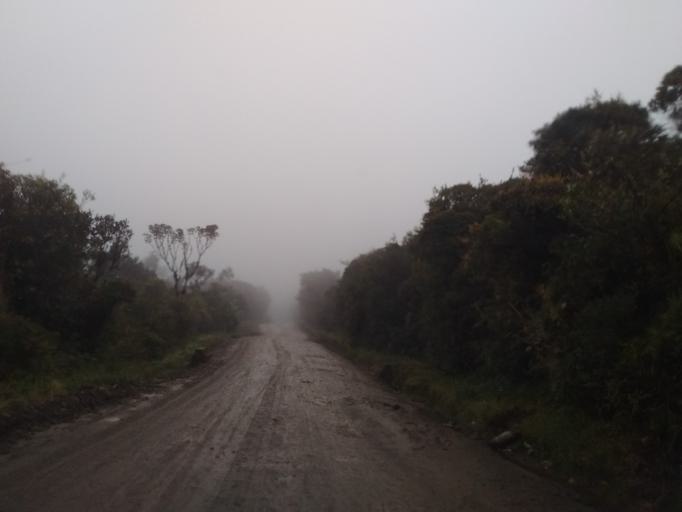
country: CO
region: Cauca
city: Paispamba
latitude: 2.1460
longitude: -76.4339
